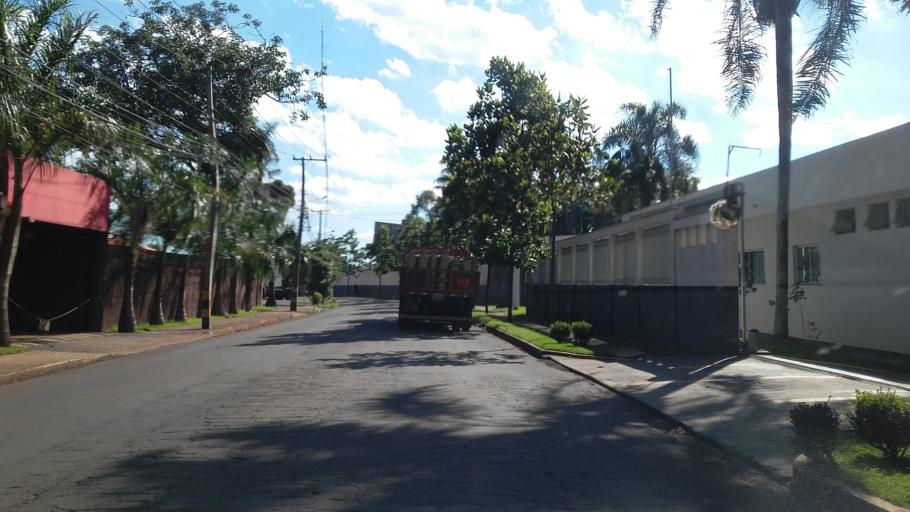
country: BR
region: Parana
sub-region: Londrina
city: Londrina
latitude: -23.2929
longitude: -51.2084
